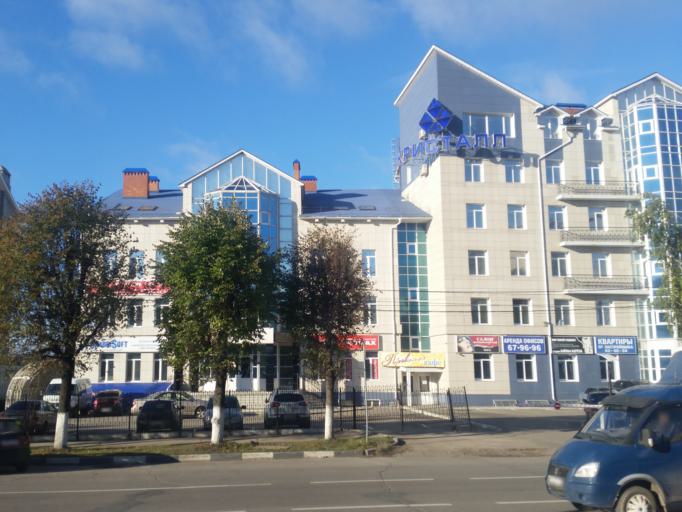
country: RU
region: Ulyanovsk
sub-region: Ulyanovskiy Rayon
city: Ulyanovsk
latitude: 54.3337
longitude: 48.3849
